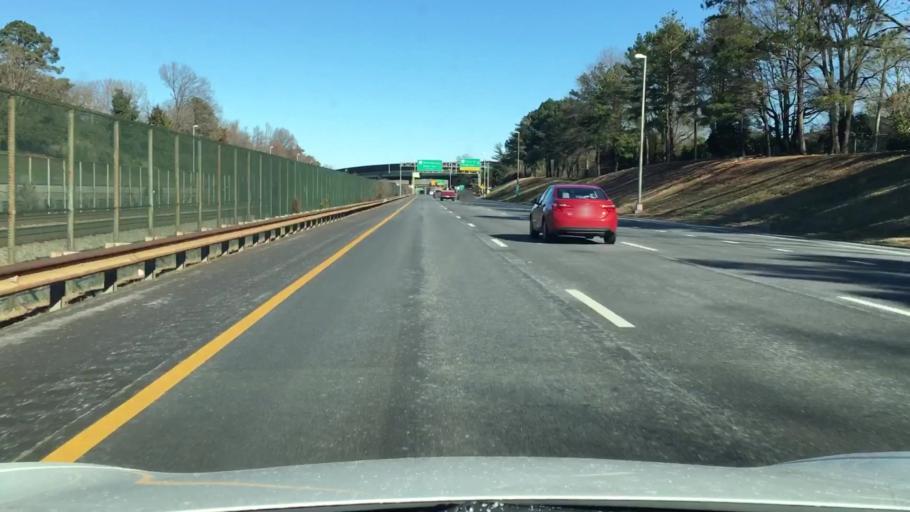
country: US
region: Virginia
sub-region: City of Richmond
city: Richmond
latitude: 37.5507
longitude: -77.4909
